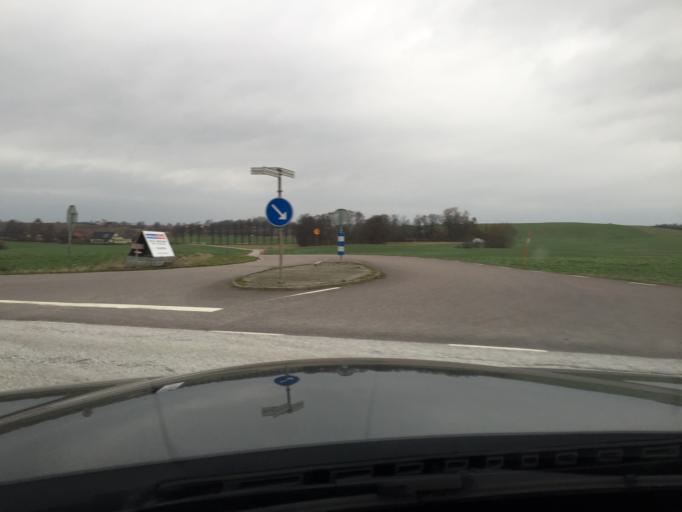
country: SE
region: Skane
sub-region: Malmo
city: Oxie
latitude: 55.5784
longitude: 13.1561
